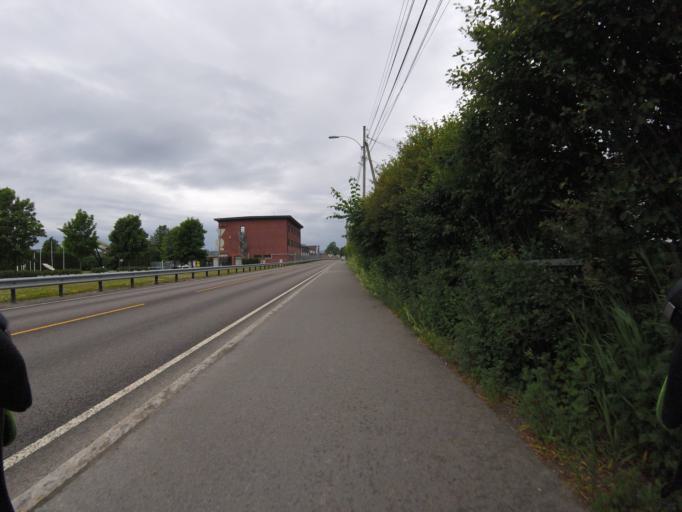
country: NO
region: Akershus
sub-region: Skedsmo
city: Lillestrom
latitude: 59.9731
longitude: 11.0404
